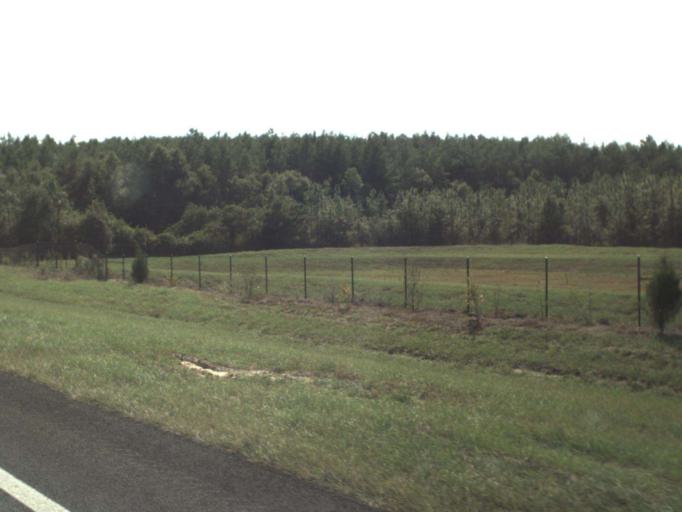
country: US
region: Florida
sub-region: Bay County
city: Laguna Beach
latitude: 30.5139
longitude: -85.8419
